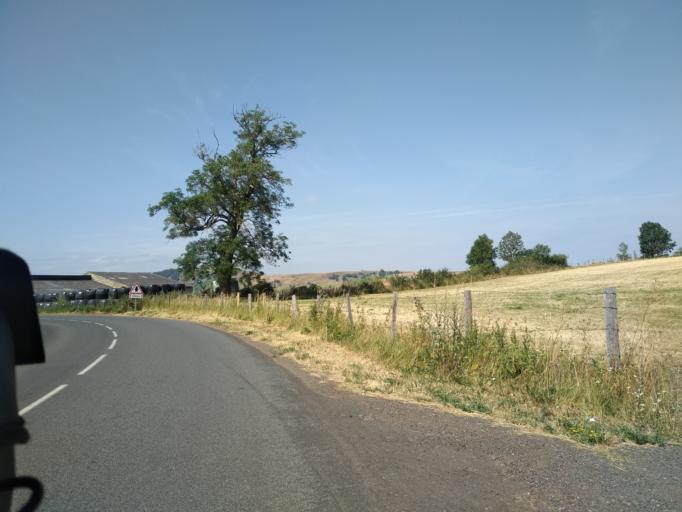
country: FR
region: Auvergne
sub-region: Departement du Cantal
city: Riom-es-Montagnes
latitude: 45.2288
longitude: 2.7271
